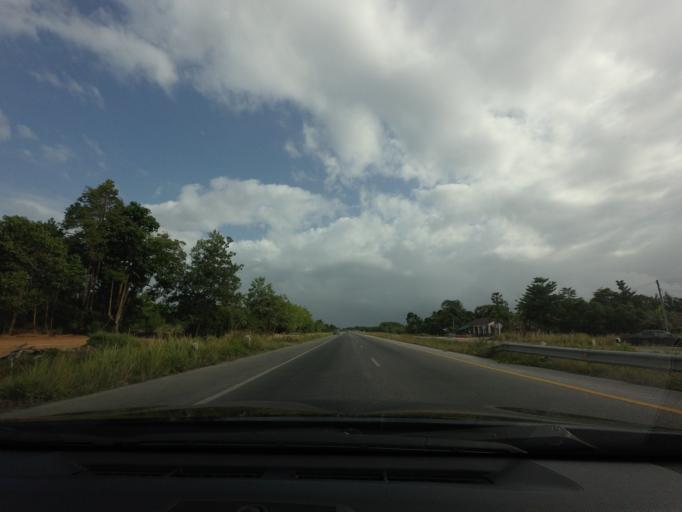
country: TH
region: Pattani
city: Mae Lan
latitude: 6.6632
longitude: 101.2351
